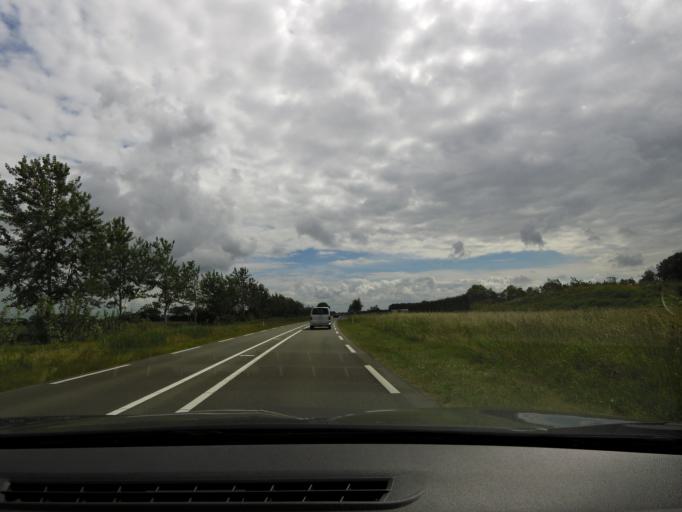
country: NL
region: Zeeland
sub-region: Gemeente Vlissingen
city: Vlissingen
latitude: 51.4804
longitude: 3.5664
